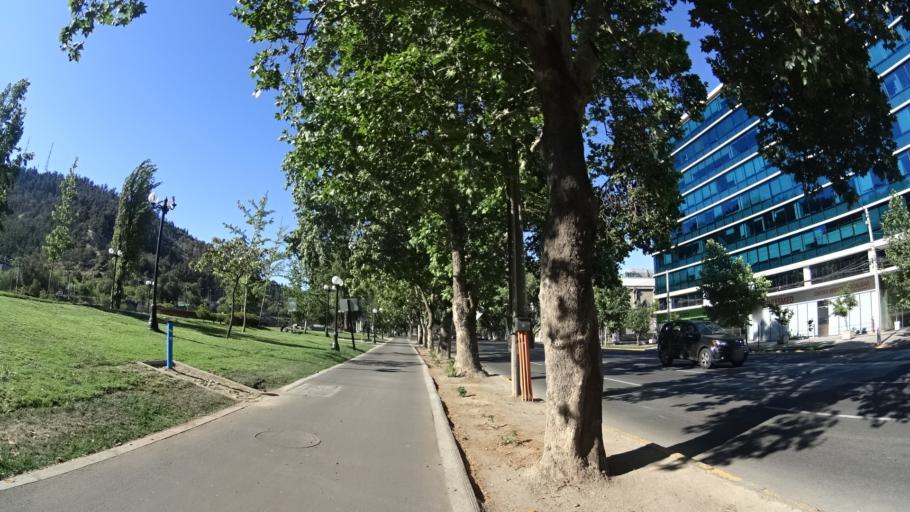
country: CL
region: Santiago Metropolitan
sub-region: Provincia de Santiago
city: Santiago
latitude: -33.4282
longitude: -70.6229
